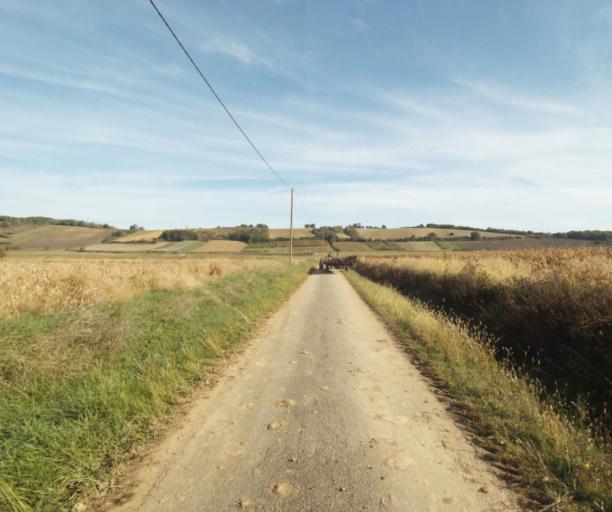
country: FR
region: Midi-Pyrenees
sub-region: Departement du Tarn-et-Garonne
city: Orgueil
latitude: 43.9183
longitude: 1.4319
